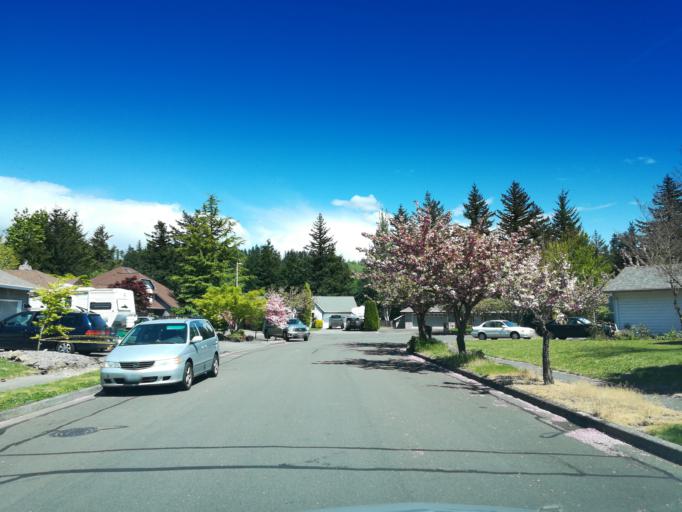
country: US
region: Oregon
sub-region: Multnomah County
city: Troutdale
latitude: 45.5319
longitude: -122.3777
